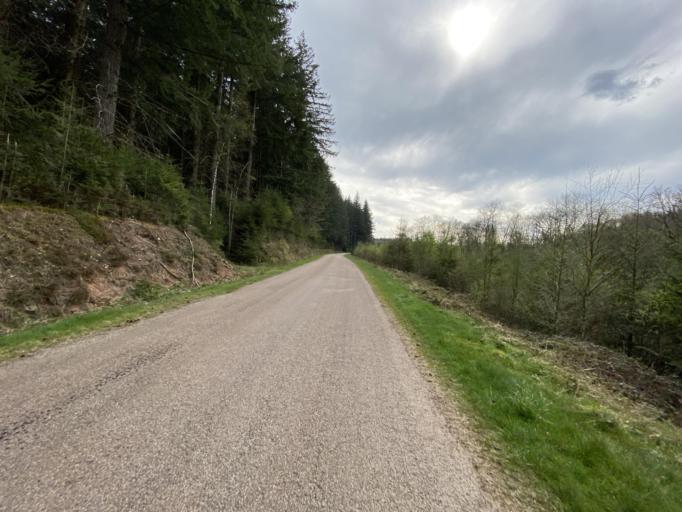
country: FR
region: Bourgogne
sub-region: Departement de la Cote-d'Or
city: Saulieu
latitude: 47.3140
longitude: 4.0931
